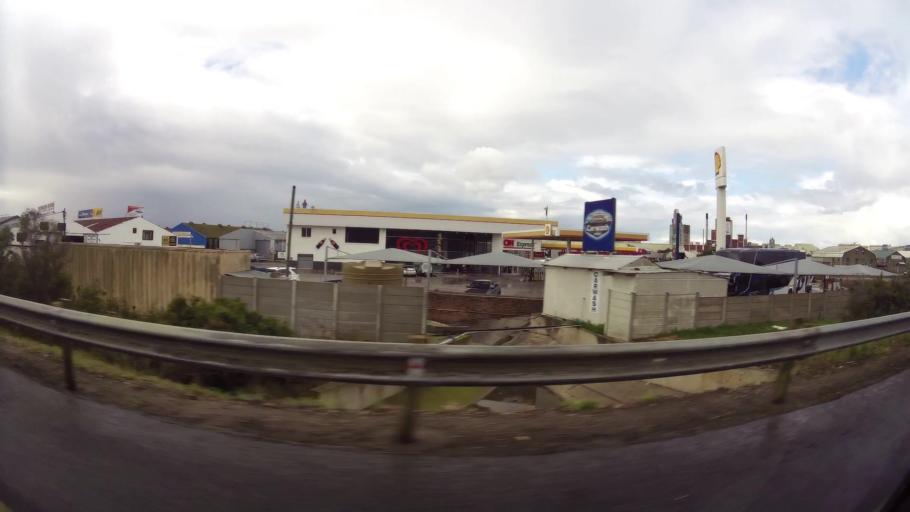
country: ZA
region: Western Cape
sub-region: Eden District Municipality
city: Mossel Bay
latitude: -34.1450
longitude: 22.1005
